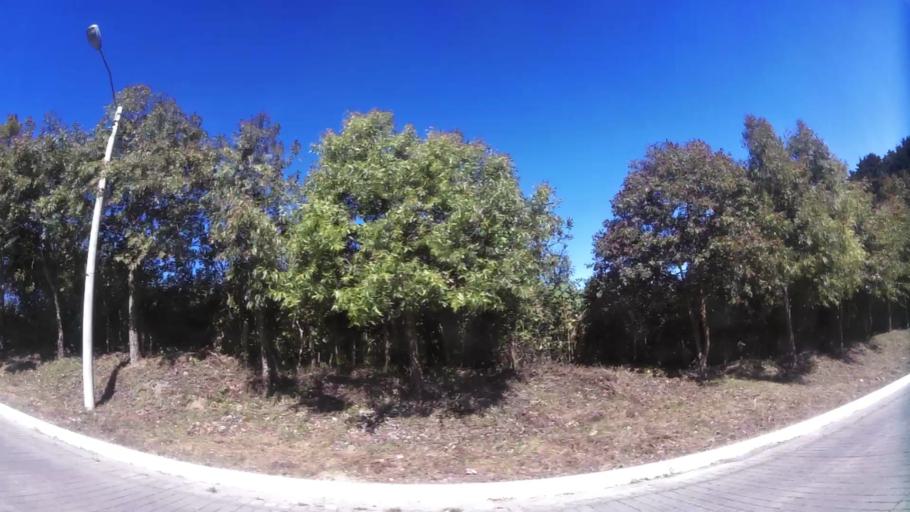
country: GT
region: Guatemala
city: San Jose Pinula
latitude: 14.5161
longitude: -90.4458
